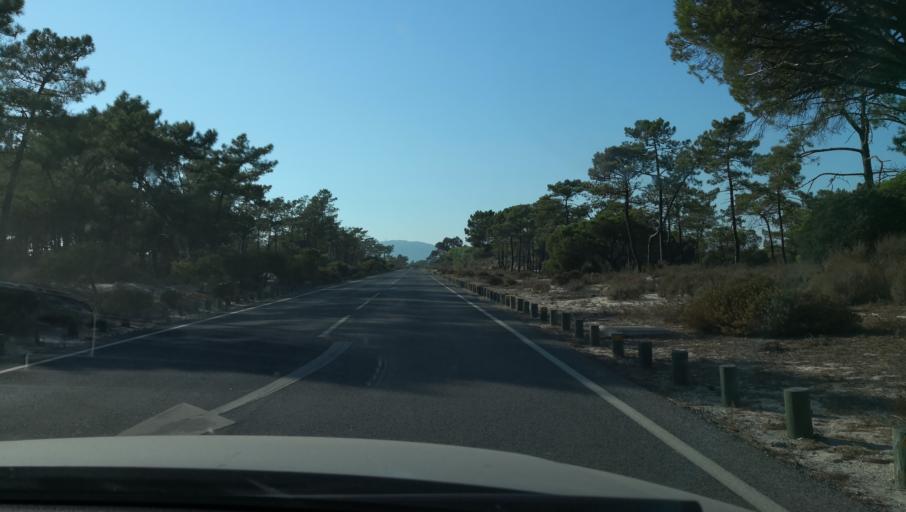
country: PT
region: Setubal
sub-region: Setubal
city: Setubal
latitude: 38.4671
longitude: -8.8768
